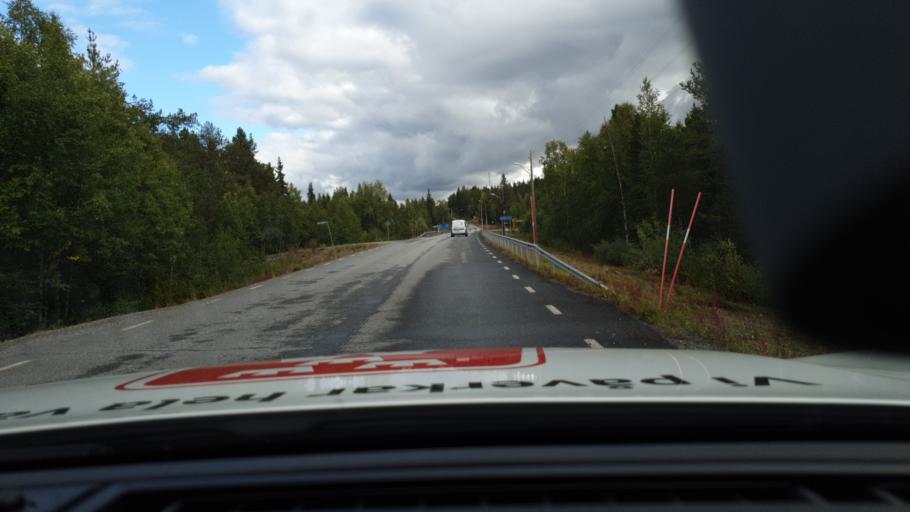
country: SE
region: Norrbotten
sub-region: Gallivare Kommun
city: Gaellivare
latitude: 66.7594
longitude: 21.0191
